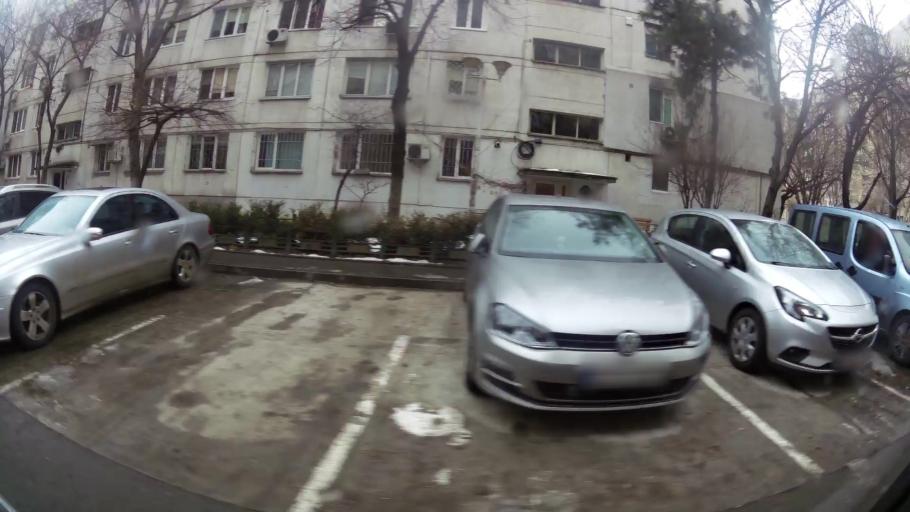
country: RO
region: Ilfov
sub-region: Comuna Chiajna
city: Rosu
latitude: 44.4173
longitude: 26.0335
